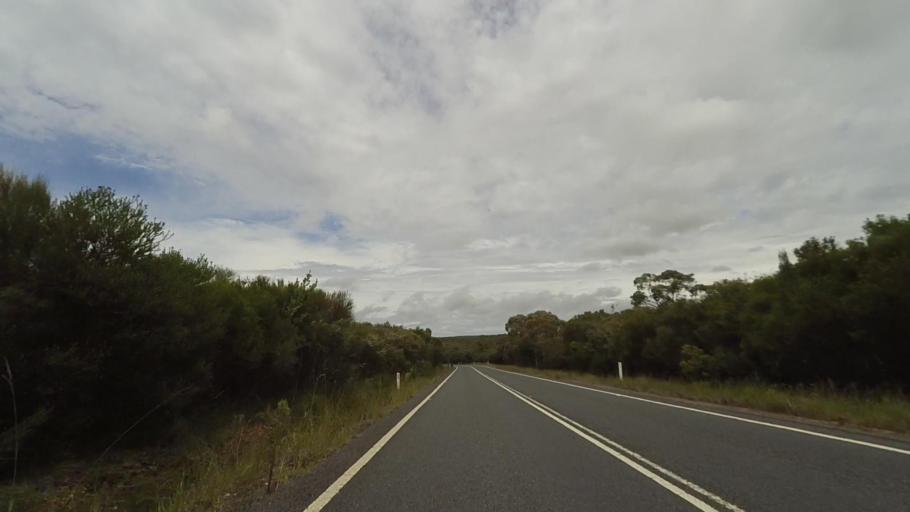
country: AU
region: New South Wales
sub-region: Sutherland Shire
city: Heathcote
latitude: -34.1111
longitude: 151.0599
